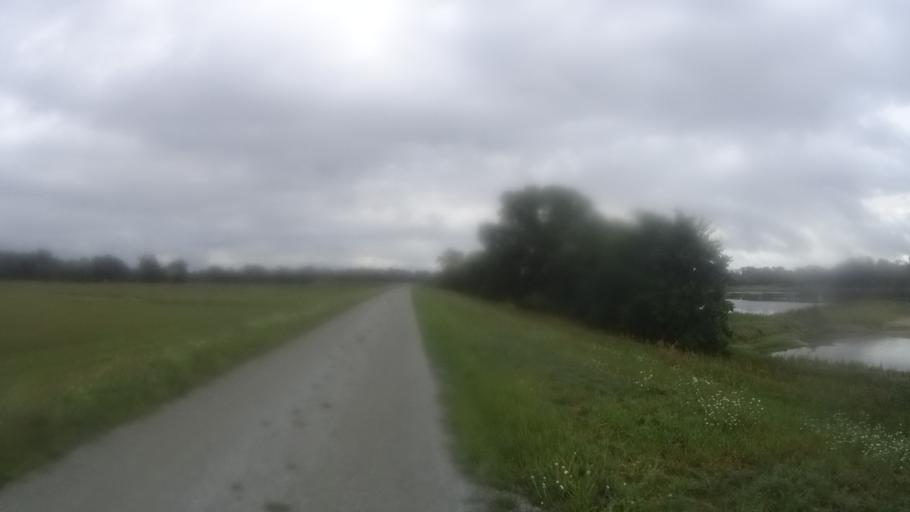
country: DE
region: Lower Saxony
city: Gorleben
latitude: 53.0582
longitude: 11.3573
